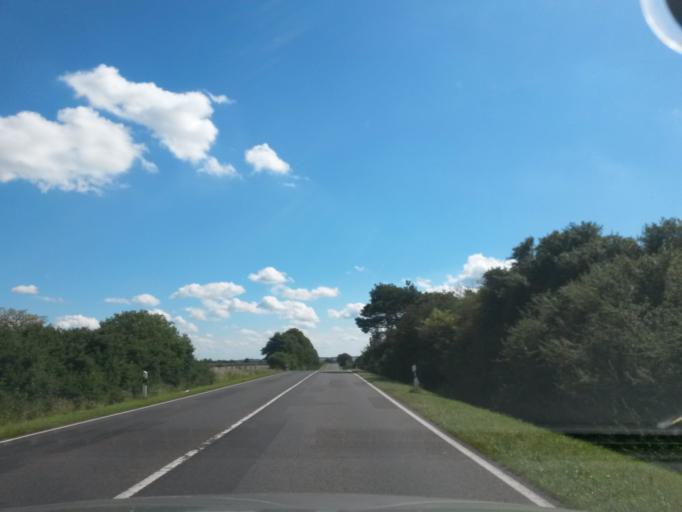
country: DE
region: Brandenburg
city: Schoneberg
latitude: 53.0304
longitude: 14.1844
